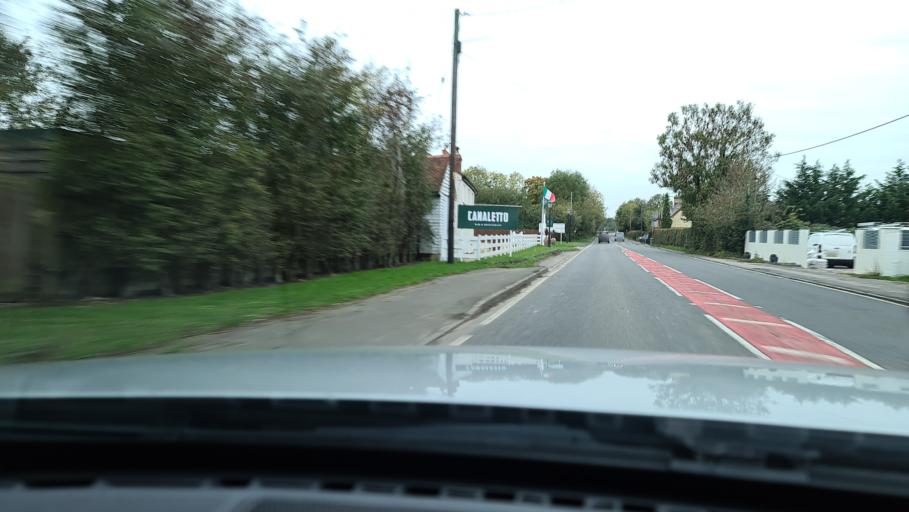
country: GB
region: England
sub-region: Buckinghamshire
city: Steeple Claydon
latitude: 51.8657
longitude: -0.9993
